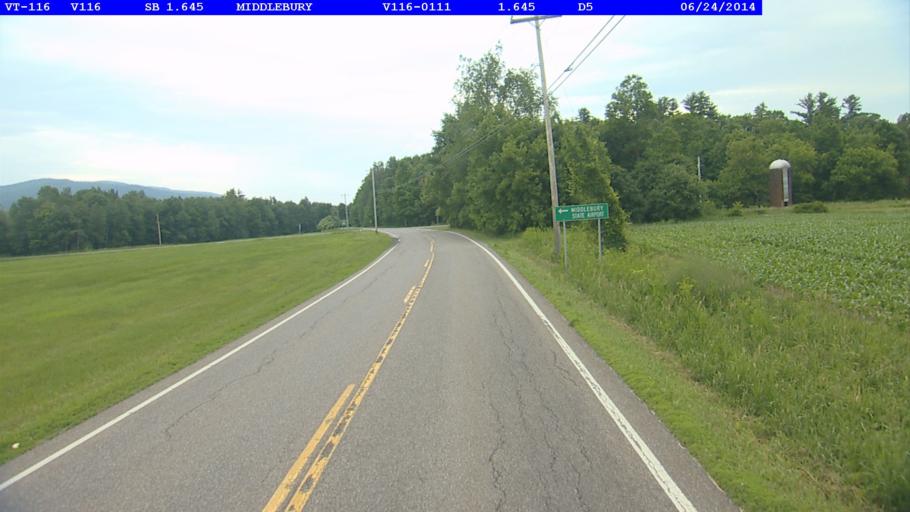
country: US
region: Vermont
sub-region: Addison County
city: Middlebury (village)
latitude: 43.9882
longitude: -73.1048
